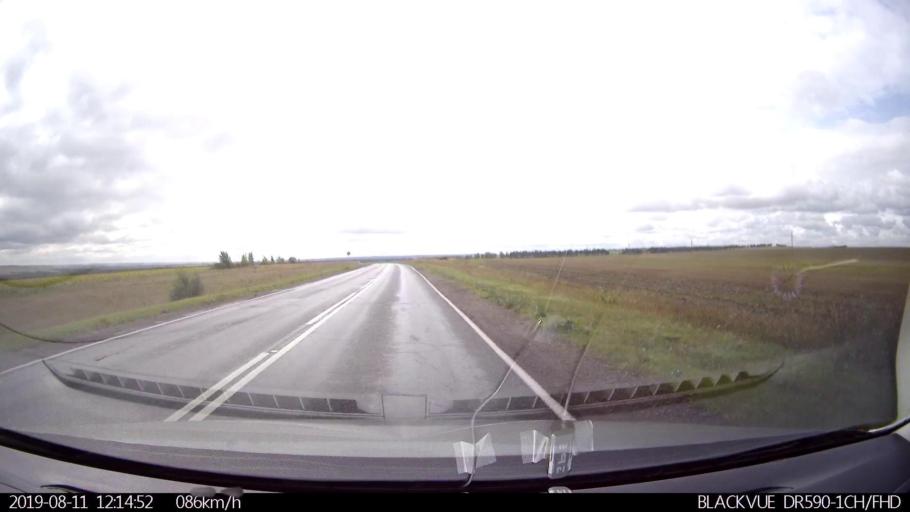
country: RU
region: Ulyanovsk
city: Ignatovka
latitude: 53.9479
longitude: 47.9744
